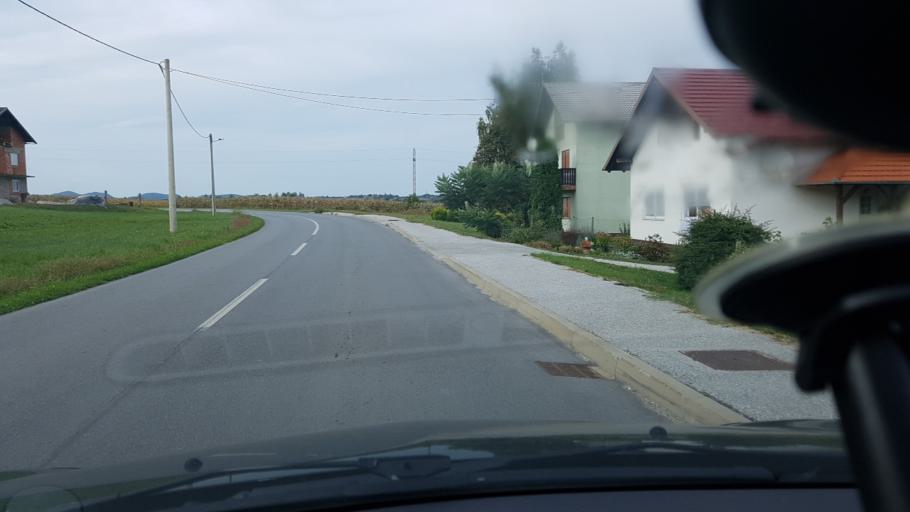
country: HR
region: Varazdinska
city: Ivanec
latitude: 46.2329
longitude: 16.1639
